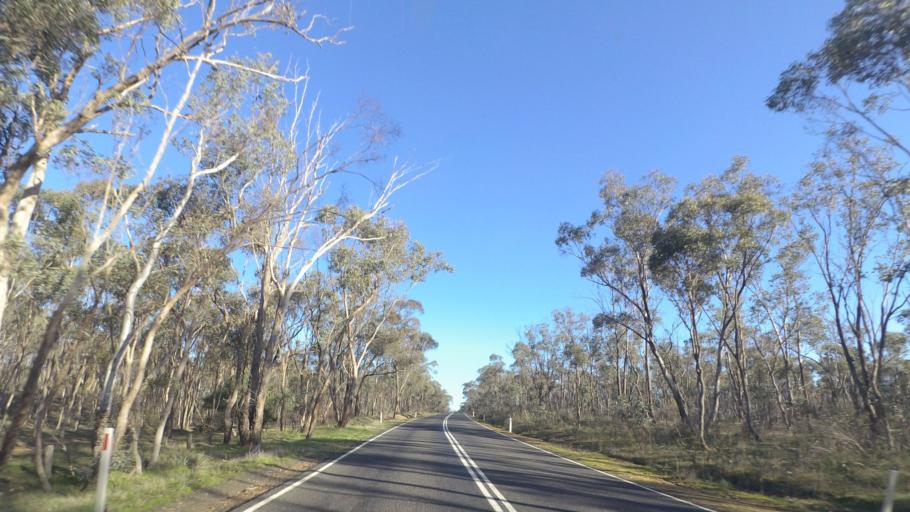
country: AU
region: Victoria
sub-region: Greater Bendigo
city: Kennington
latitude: -36.9045
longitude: 144.4947
